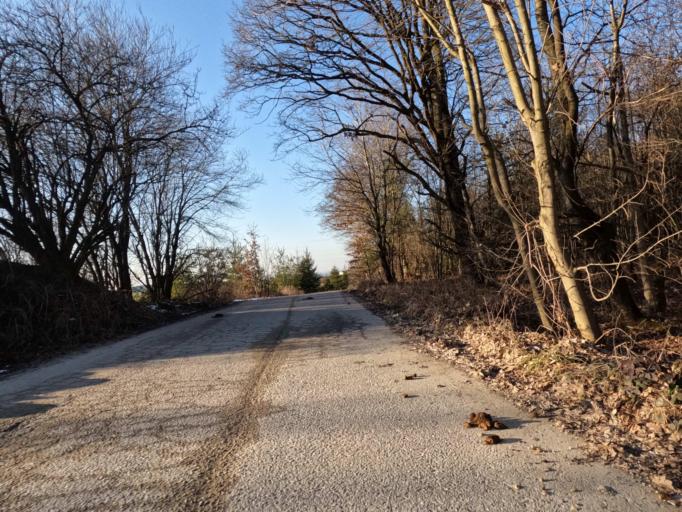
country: DE
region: Bavaria
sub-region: Upper Bavaria
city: Vachendorf
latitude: 47.8735
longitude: 12.6062
